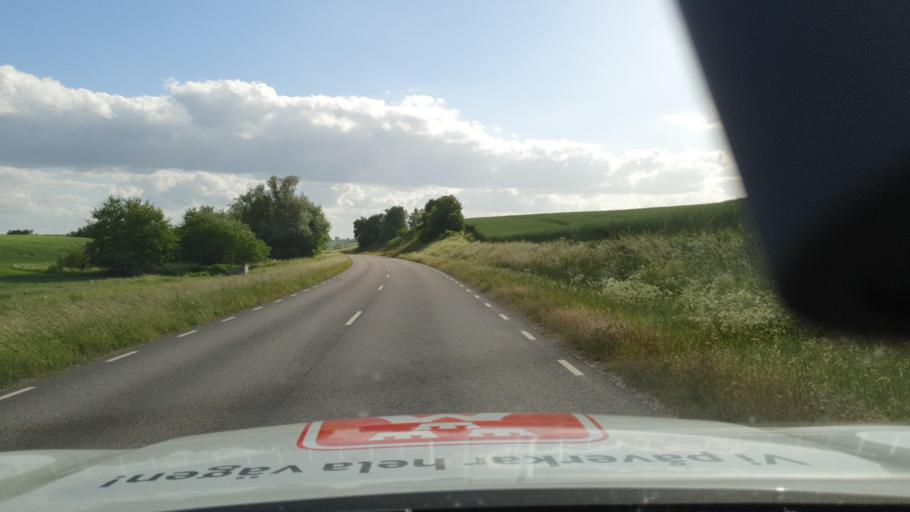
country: SE
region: Skane
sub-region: Tomelilla Kommun
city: Tomelilla
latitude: 55.5782
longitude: 14.0073
